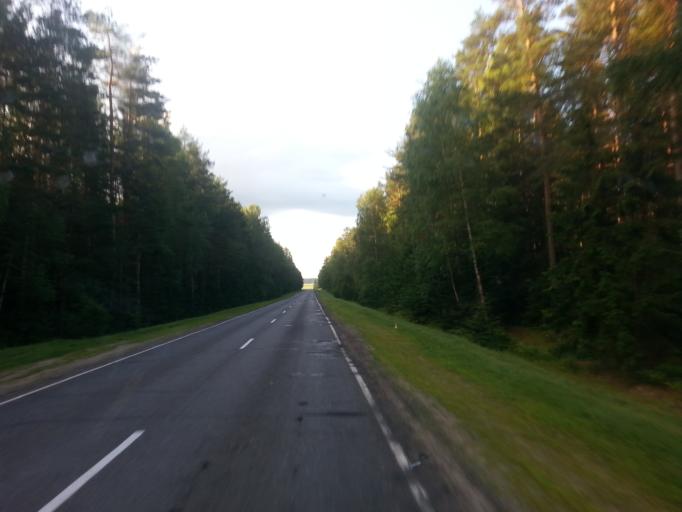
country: BY
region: Minsk
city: Il'ya
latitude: 54.4868
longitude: 27.2417
